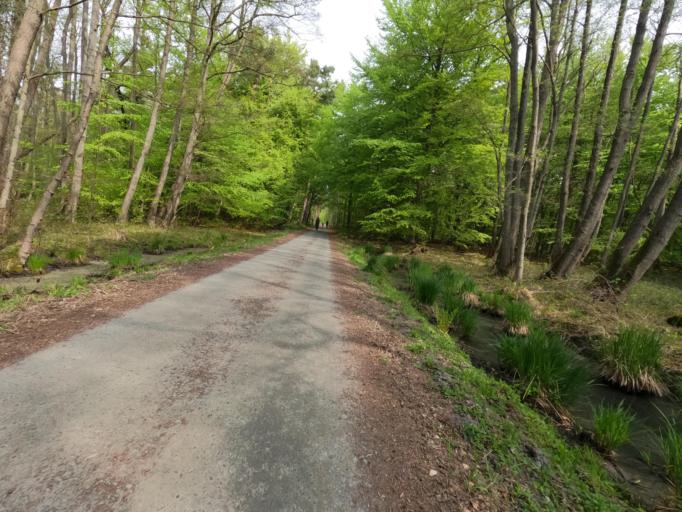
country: DE
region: Mecklenburg-Vorpommern
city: Ostseebad Prerow
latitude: 54.4617
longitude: 12.5150
